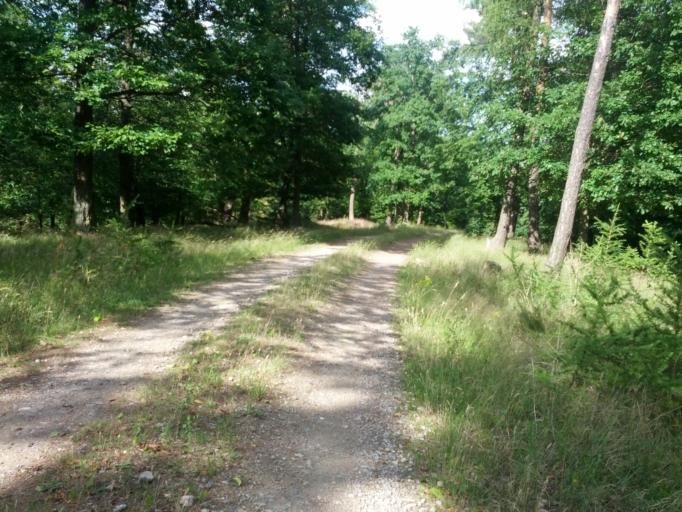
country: DE
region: Thuringia
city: Wolfsburg-Unkeroda
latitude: 50.9693
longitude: 10.2586
